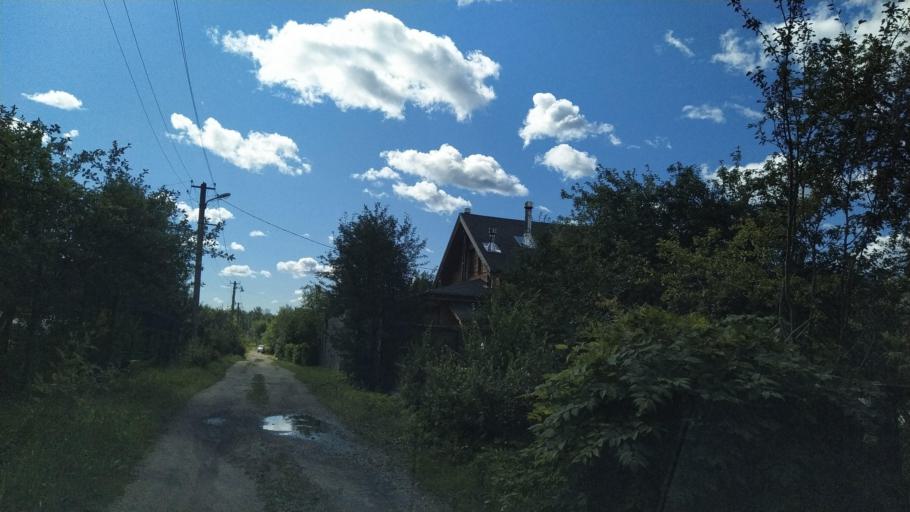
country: RU
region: Leningrad
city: Priozersk
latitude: 61.0016
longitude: 30.1709
